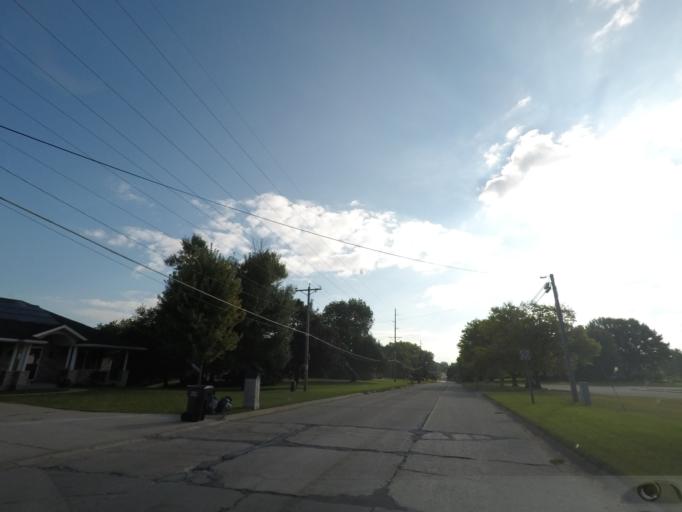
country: US
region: Iowa
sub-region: Story County
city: Nevada
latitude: 42.0155
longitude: -93.4627
